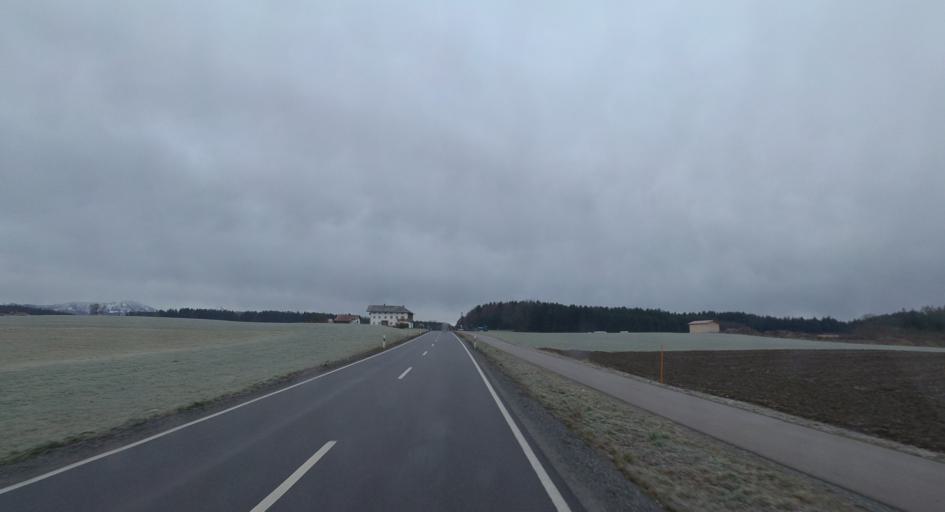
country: DE
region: Bavaria
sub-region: Upper Bavaria
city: Nussdorf
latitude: 47.9283
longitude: 12.5903
